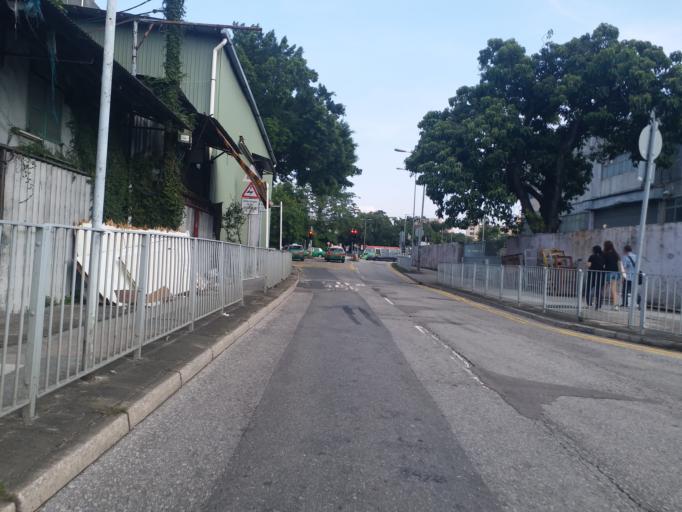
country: HK
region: Yuen Long
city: Yuen Long Kau Hui
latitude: 22.4431
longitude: 114.0109
